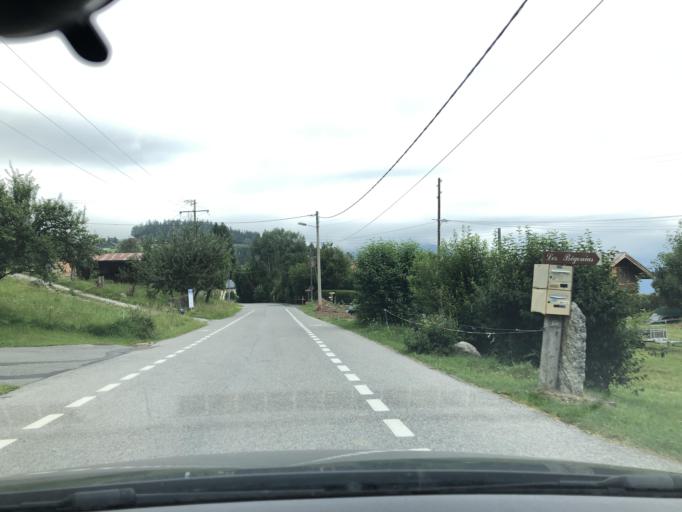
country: FR
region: Rhone-Alpes
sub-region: Departement de la Haute-Savoie
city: Combloux
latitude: 45.8977
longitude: 6.6349
